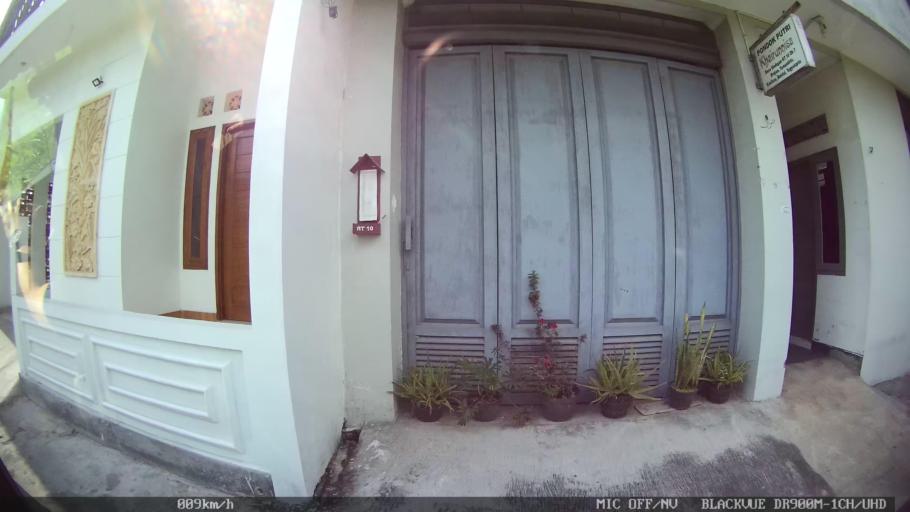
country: ID
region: Daerah Istimewa Yogyakarta
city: Kasihan
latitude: -7.8120
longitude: 110.3291
